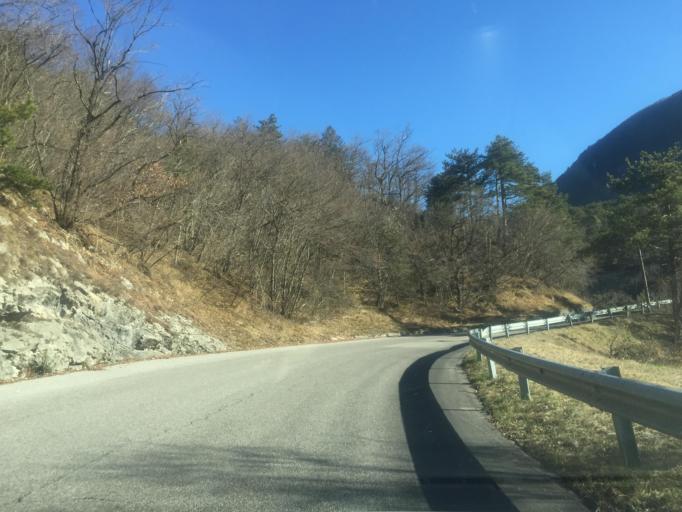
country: IT
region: Friuli Venezia Giulia
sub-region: Provincia di Udine
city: Tolmezzo
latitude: 46.4120
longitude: 13.0433
